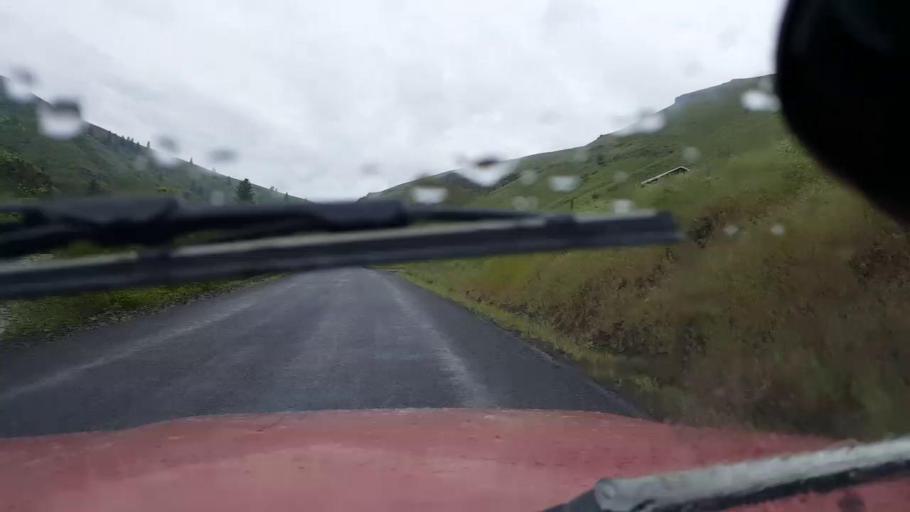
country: US
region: Washington
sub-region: Asotin County
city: Asotin
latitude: 46.0260
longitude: -117.3344
